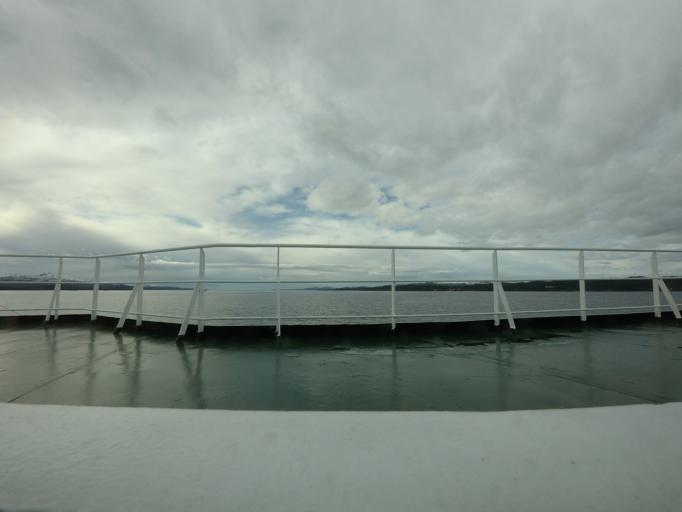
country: NO
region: Sor-Trondelag
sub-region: Hitra
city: Fillan
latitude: 63.4802
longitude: 8.9845
